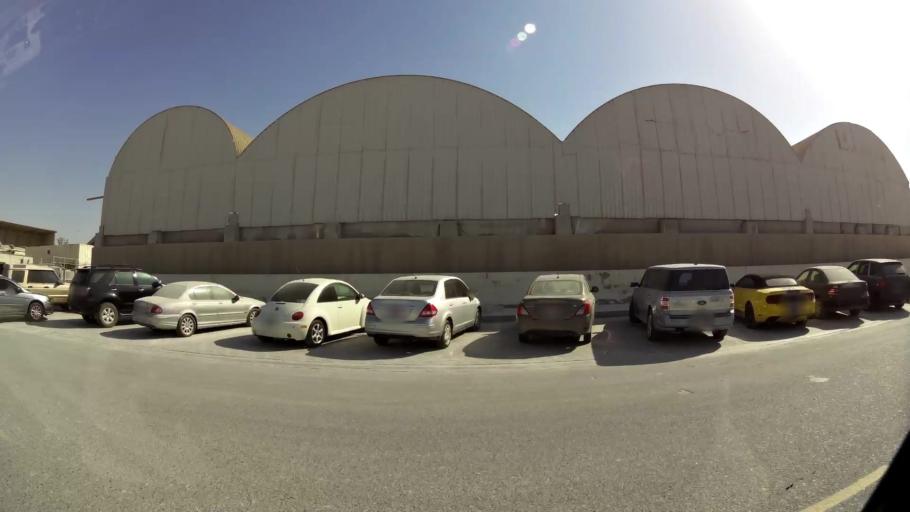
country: AE
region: Dubai
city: Dubai
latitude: 25.1356
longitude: 55.2210
